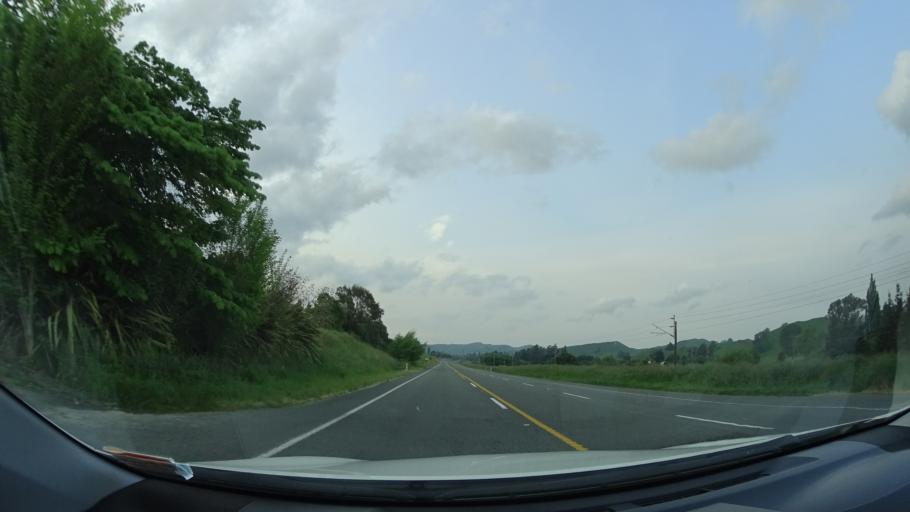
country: NZ
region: Manawatu-Wanganui
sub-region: Ruapehu District
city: Waiouru
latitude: -39.7242
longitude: 175.8416
